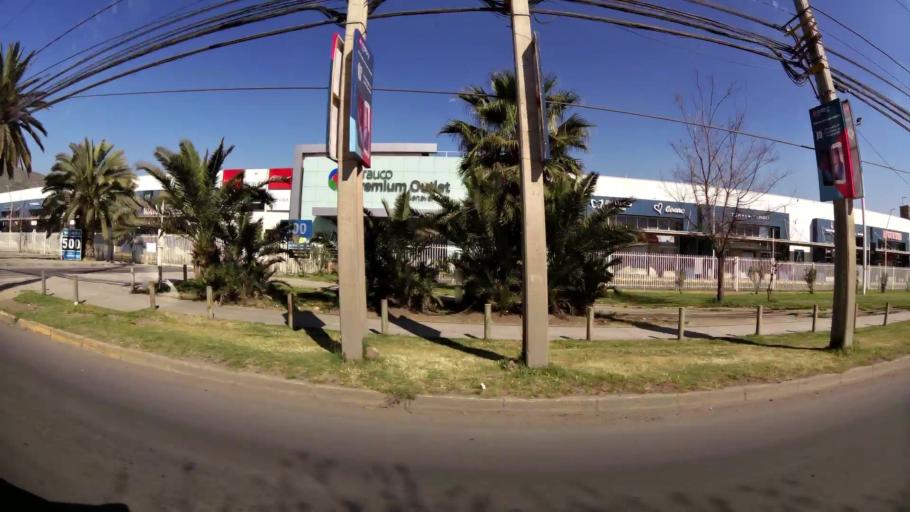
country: CL
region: Santiago Metropolitan
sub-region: Provincia de Chacabuco
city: Chicureo Abajo
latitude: -33.3311
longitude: -70.7050
